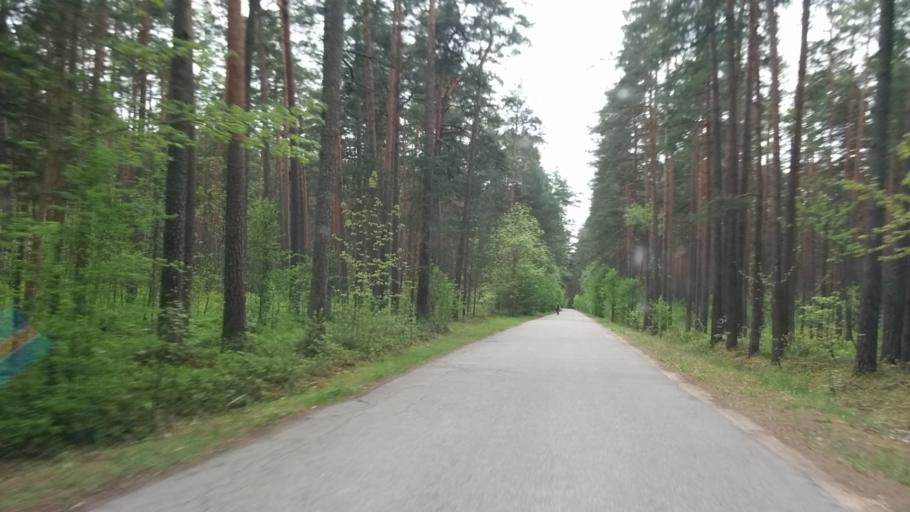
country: LV
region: Babite
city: Pinki
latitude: 56.9391
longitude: 23.9349
